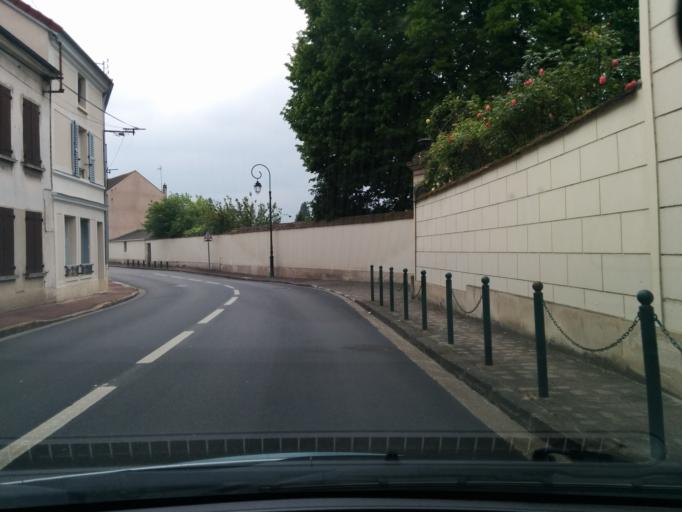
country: FR
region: Ile-de-France
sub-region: Departement des Yvelines
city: Vaux-sur-Seine
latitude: 49.0079
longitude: 1.9583
